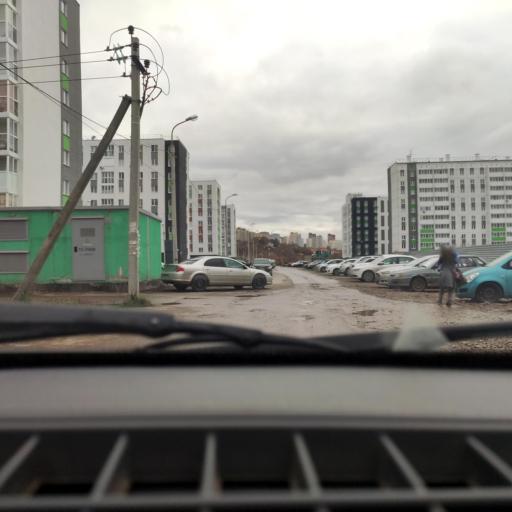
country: RU
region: Bashkortostan
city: Ufa
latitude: 54.6936
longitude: 55.9697
